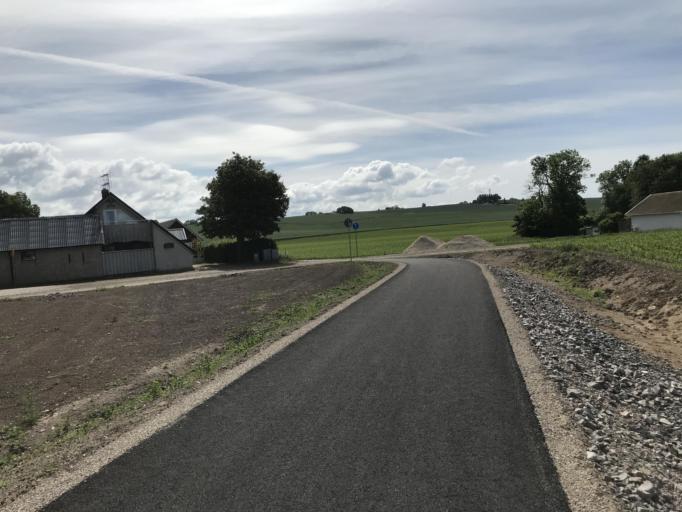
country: SE
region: Skane
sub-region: Helsingborg
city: Glumslov
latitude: 55.9427
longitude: 12.7887
